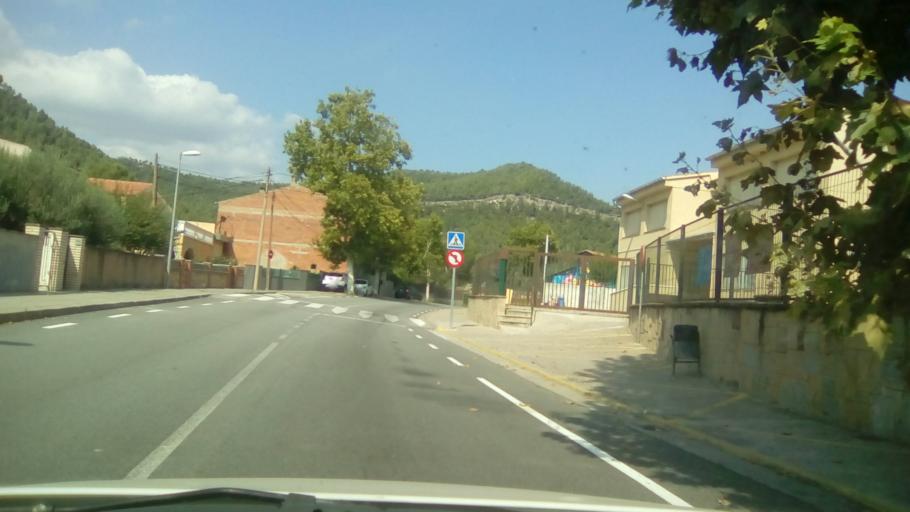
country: ES
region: Catalonia
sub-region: Provincia de Barcelona
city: Monistrol de Montserrat
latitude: 41.6325
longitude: 1.8537
